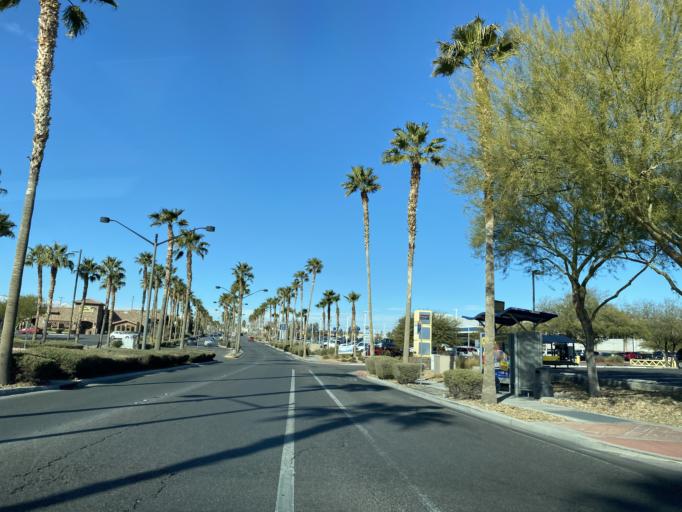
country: US
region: Nevada
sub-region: Clark County
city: Las Vegas
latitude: 36.2723
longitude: -115.2649
